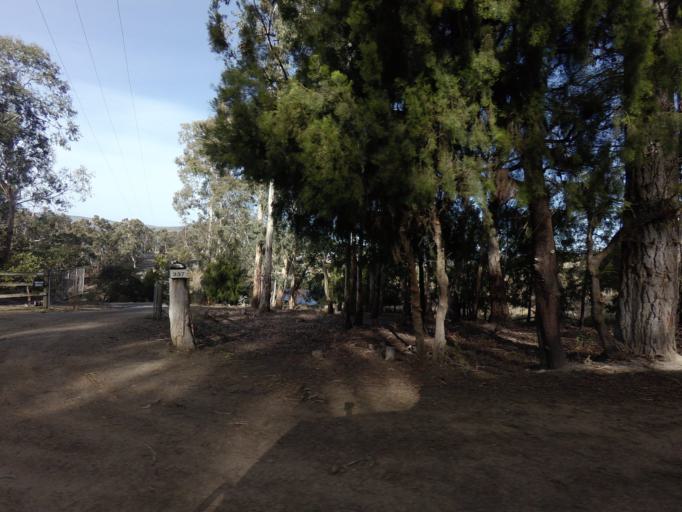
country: AU
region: Tasmania
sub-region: Kingborough
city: Kettering
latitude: -43.1188
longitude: 147.2653
